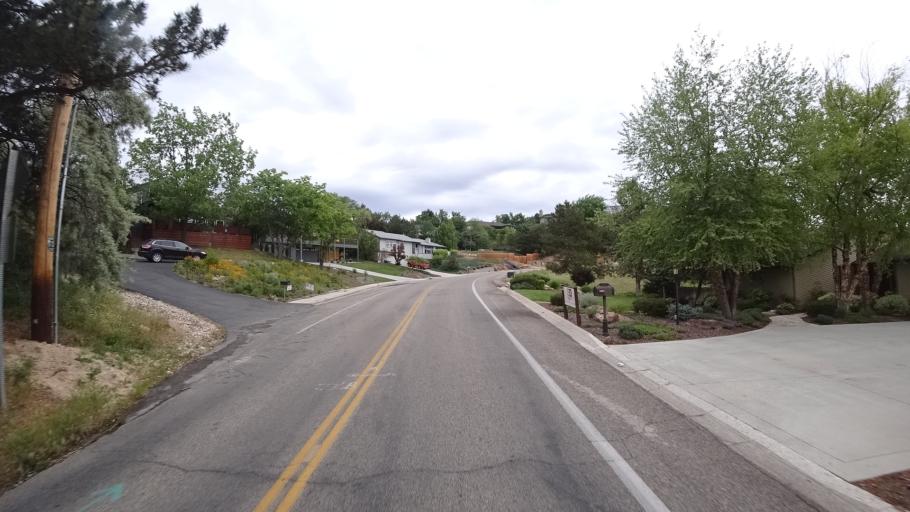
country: US
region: Idaho
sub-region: Ada County
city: Boise
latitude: 43.6152
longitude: -116.1779
